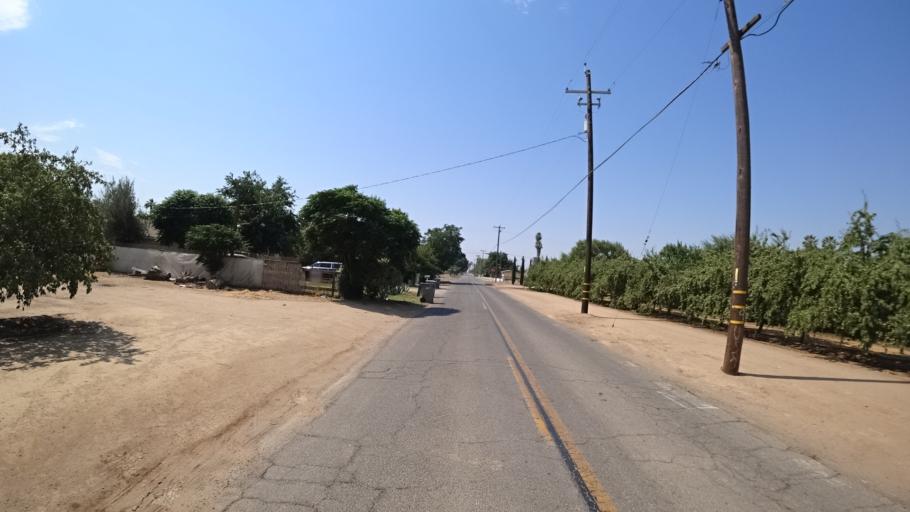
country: US
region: California
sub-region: Fresno County
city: West Park
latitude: 36.7290
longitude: -119.8534
